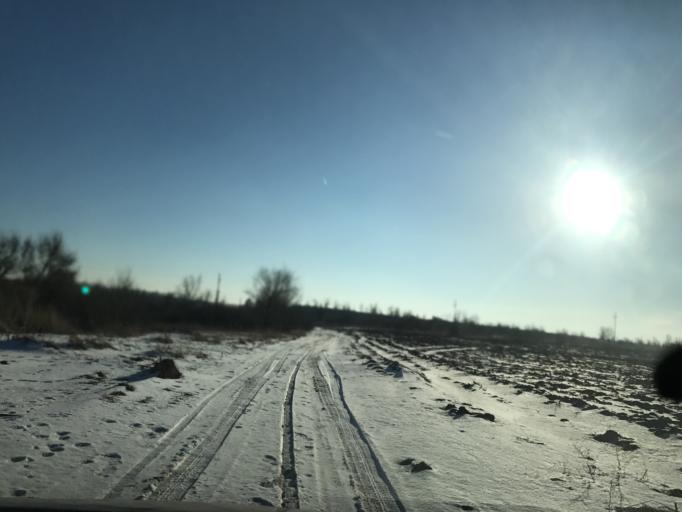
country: RU
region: Rostov
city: Staraya Stanitsa
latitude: 48.2368
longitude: 40.3942
